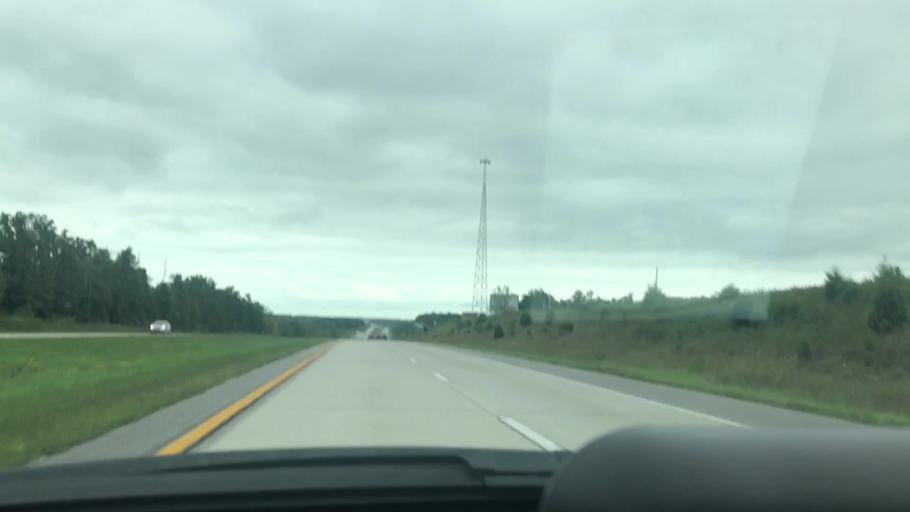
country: US
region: Missouri
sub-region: Greene County
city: Fair Grove
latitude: 37.5065
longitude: -93.1388
